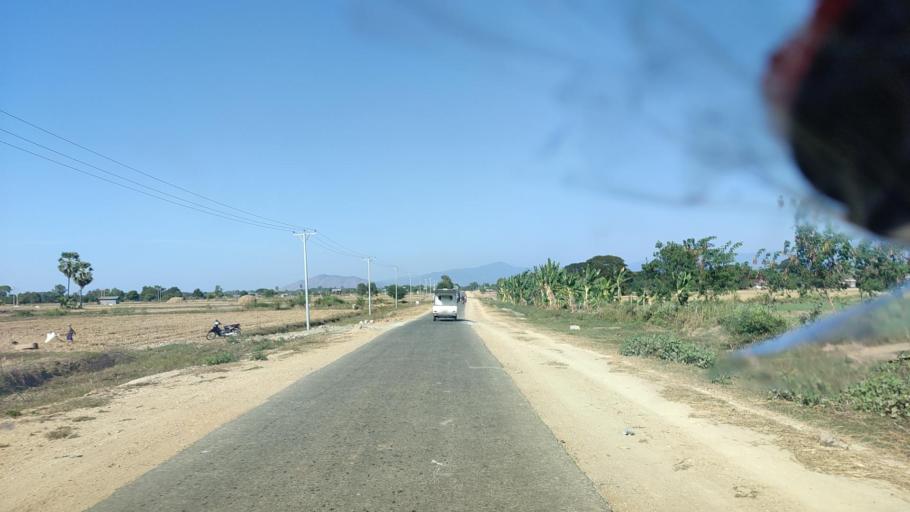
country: MM
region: Mandalay
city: Yamethin
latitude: 20.1625
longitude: 96.2585
